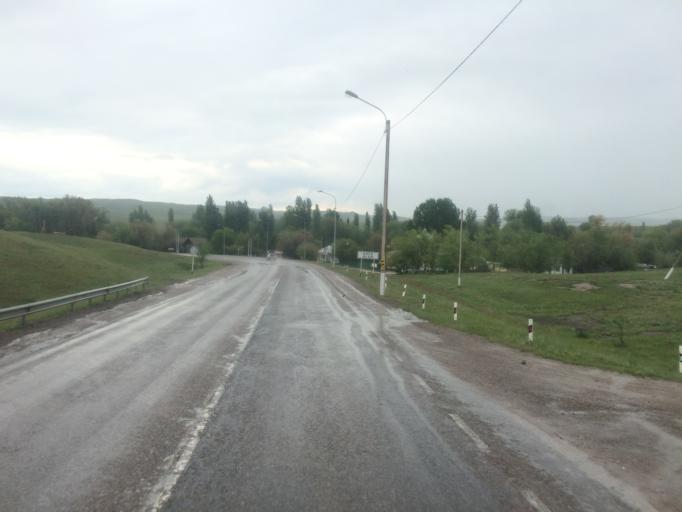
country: KZ
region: Zhambyl
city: Georgiyevka
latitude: 43.2312
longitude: 74.7600
